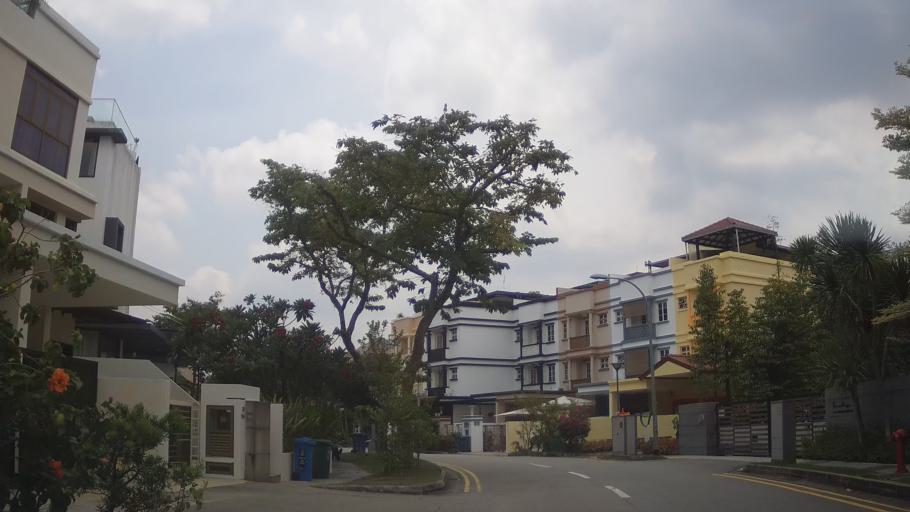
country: MY
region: Johor
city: Johor Bahru
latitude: 1.3720
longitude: 103.7693
